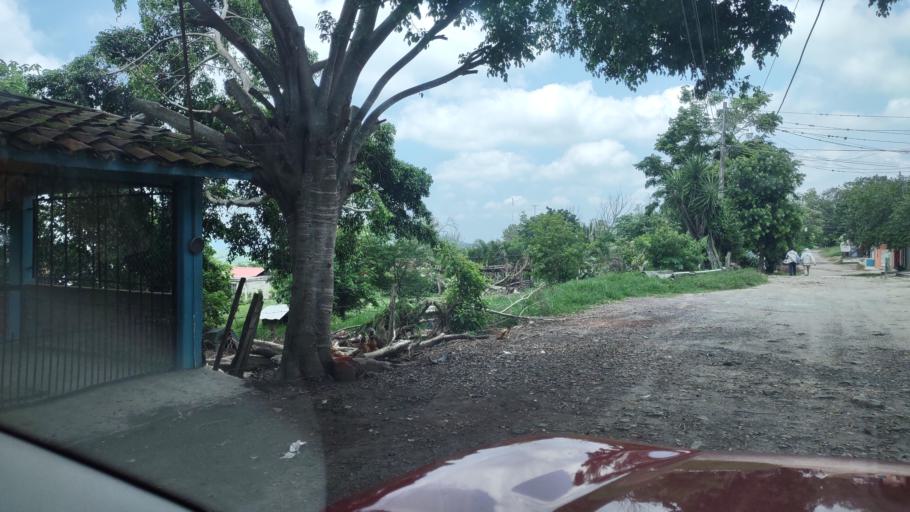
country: MX
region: Veracruz
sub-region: Emiliano Zapata
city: Dos Rios
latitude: 19.4875
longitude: -96.8136
